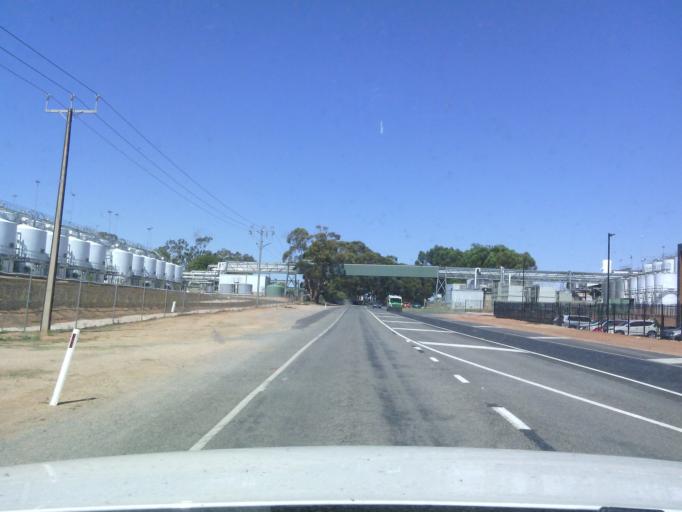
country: AU
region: South Australia
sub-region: Berri and Barmera
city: Monash
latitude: -34.2785
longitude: 140.5418
